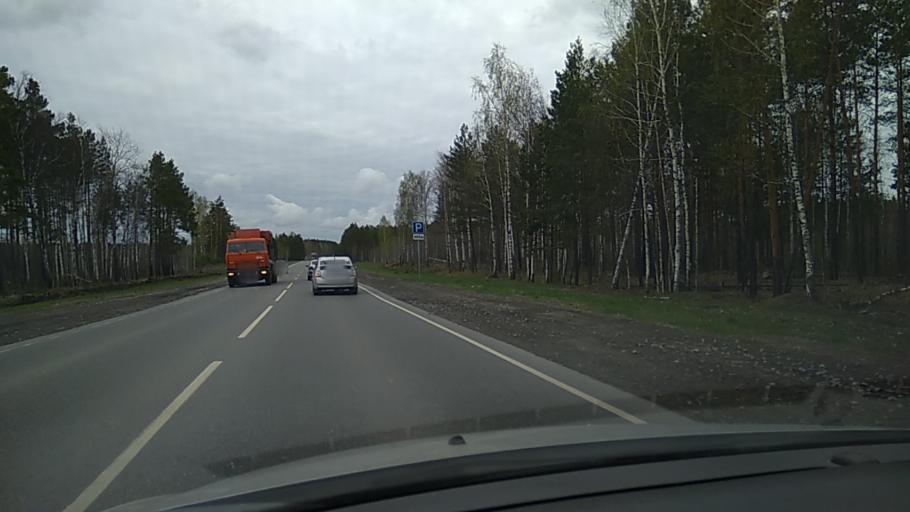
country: RU
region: Tjumen
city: Chervishevo
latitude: 56.9963
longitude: 65.4796
